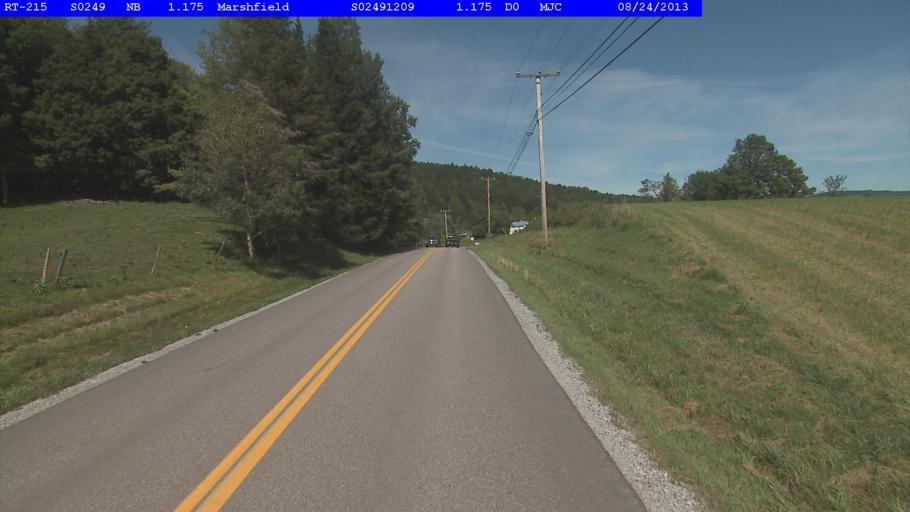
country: US
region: Vermont
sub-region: Caledonia County
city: Hardwick
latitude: 44.3645
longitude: -72.3367
